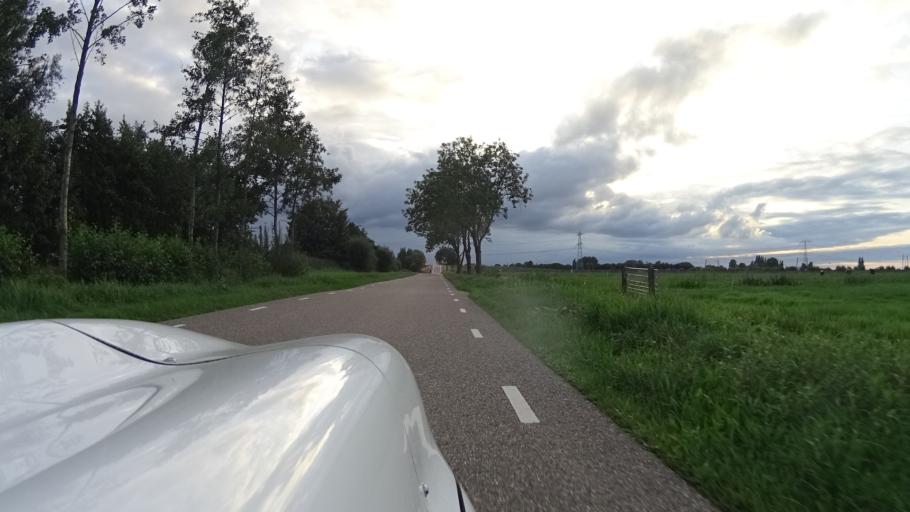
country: NL
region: South Holland
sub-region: Gemeente Sliedrecht
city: Sliedrecht
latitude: 51.8299
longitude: 4.8137
